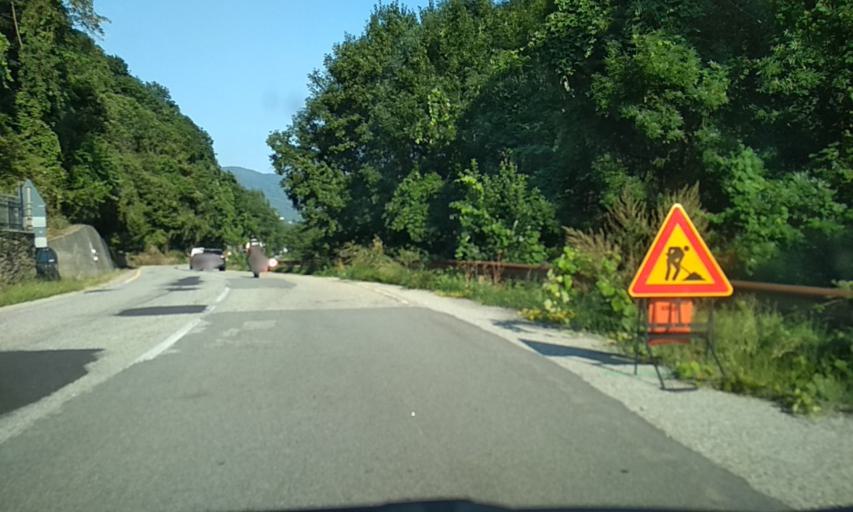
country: IT
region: Piedmont
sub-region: Provincia di Torino
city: Alpette
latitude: 45.4196
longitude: 7.5664
